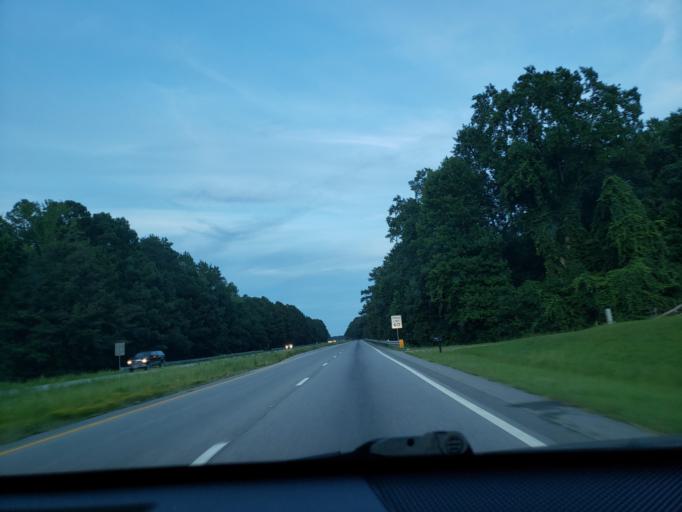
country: US
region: Virginia
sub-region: Southampton County
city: Courtland
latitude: 36.7074
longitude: -77.1574
